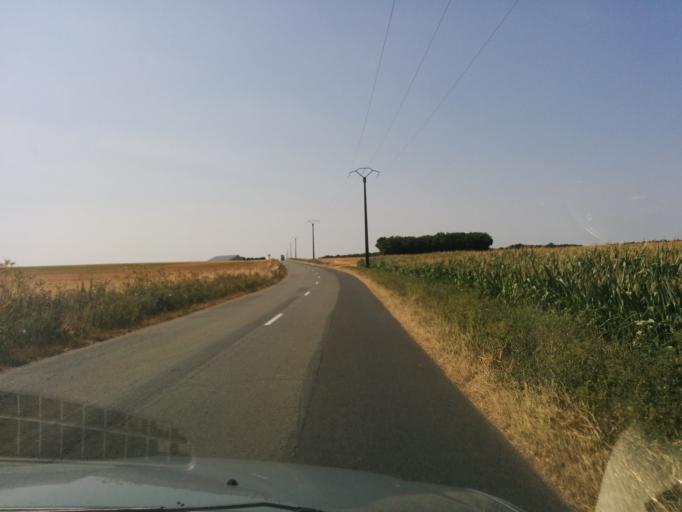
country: FR
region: Poitou-Charentes
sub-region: Departement de la Vienne
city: Mirebeau
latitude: 46.7347
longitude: 0.1904
